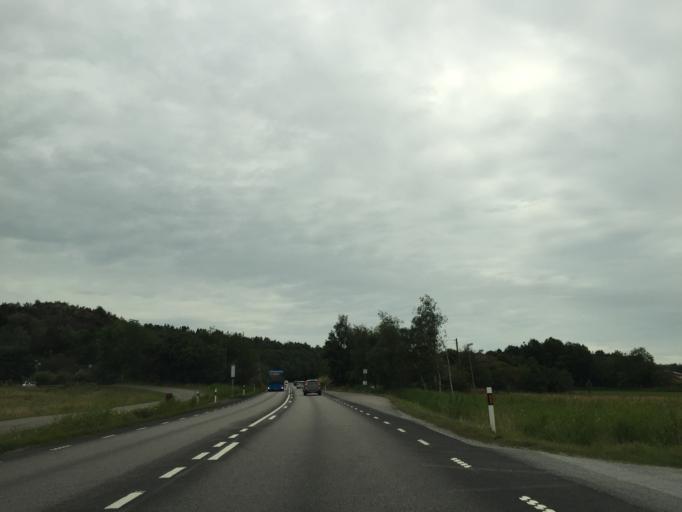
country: SE
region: Vaestra Goetaland
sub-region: Tjorns Kommun
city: Myggenas
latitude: 58.0442
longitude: 11.7438
